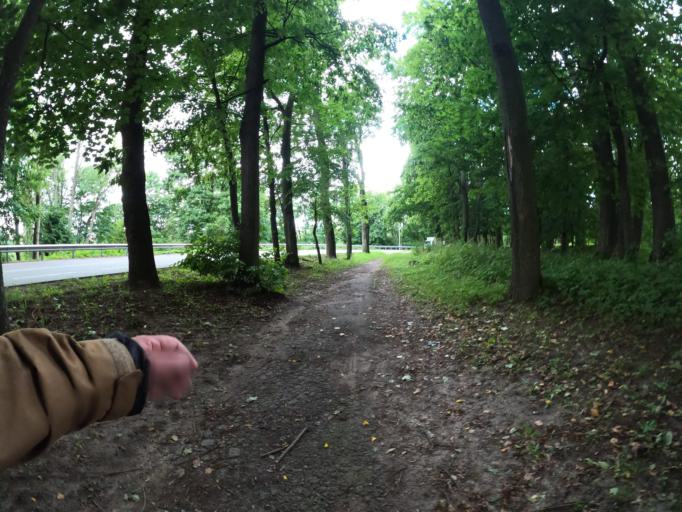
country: RU
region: Kaliningrad
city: Zheleznodorozhnyy
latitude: 54.3614
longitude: 21.3118
